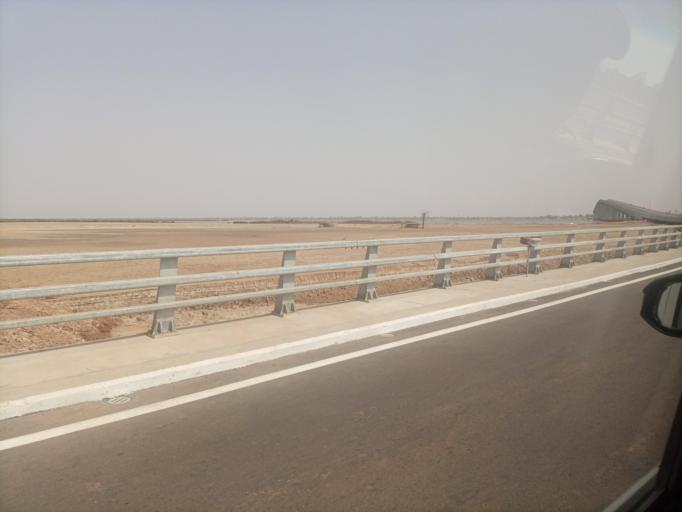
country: SN
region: Fatick
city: Foundiougne
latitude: 14.1440
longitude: -16.4721
